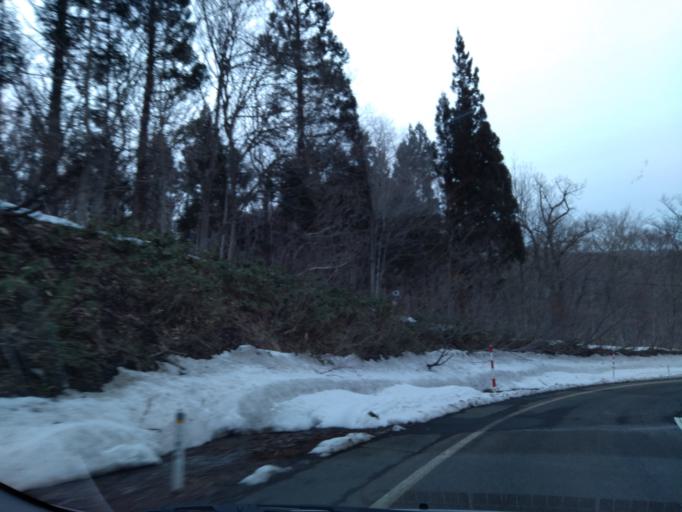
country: JP
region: Iwate
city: Kitakami
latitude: 39.2380
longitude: 140.9523
